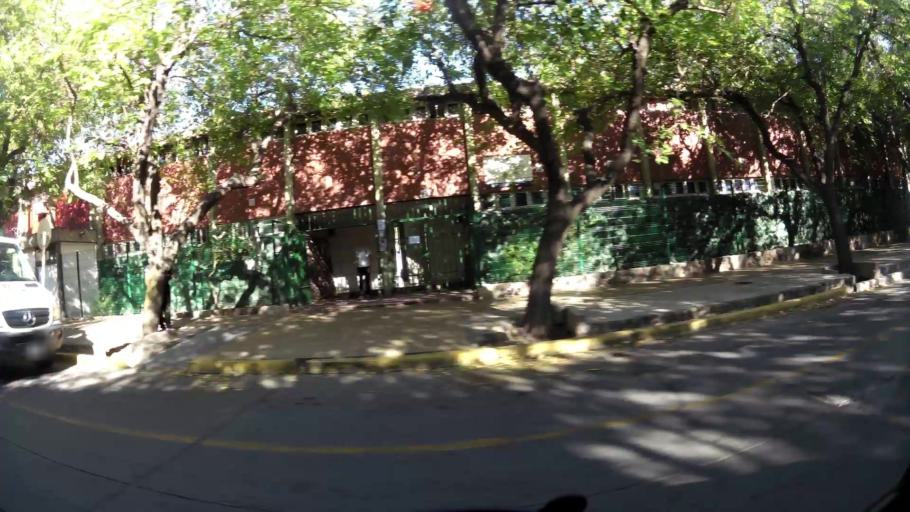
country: AR
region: Mendoza
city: Las Heras
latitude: -32.8702
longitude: -68.8368
